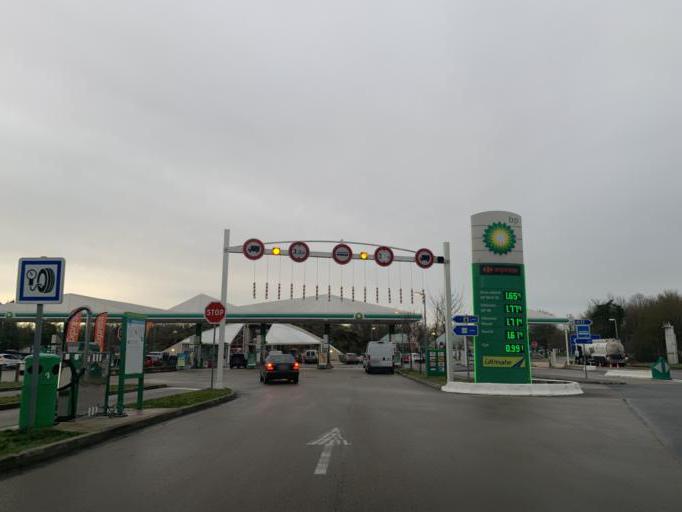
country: FR
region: Champagne-Ardenne
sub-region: Departement de la Haute-Marne
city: Chateauvillain
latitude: 48.0556
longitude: 4.9615
